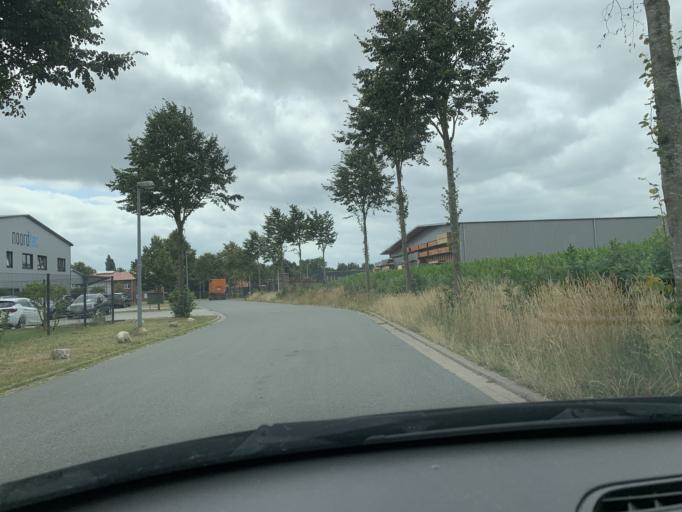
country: DE
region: Lower Saxony
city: Westerstede
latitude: 53.2672
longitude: 7.9503
